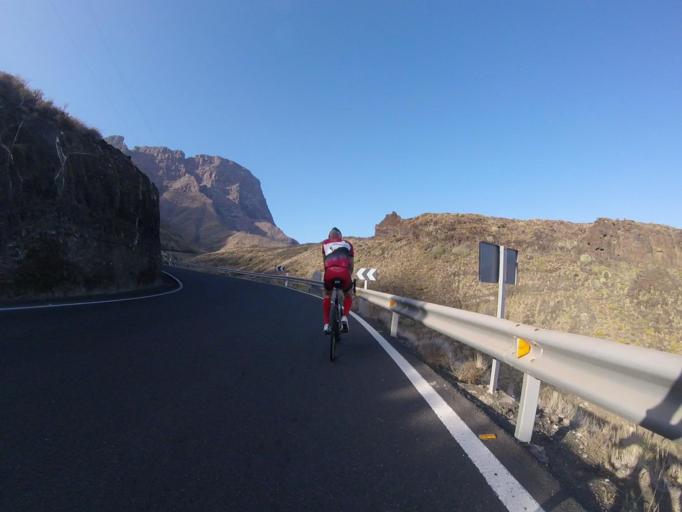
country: ES
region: Canary Islands
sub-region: Provincia de Las Palmas
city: Agaete
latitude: 28.0784
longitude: -15.7078
